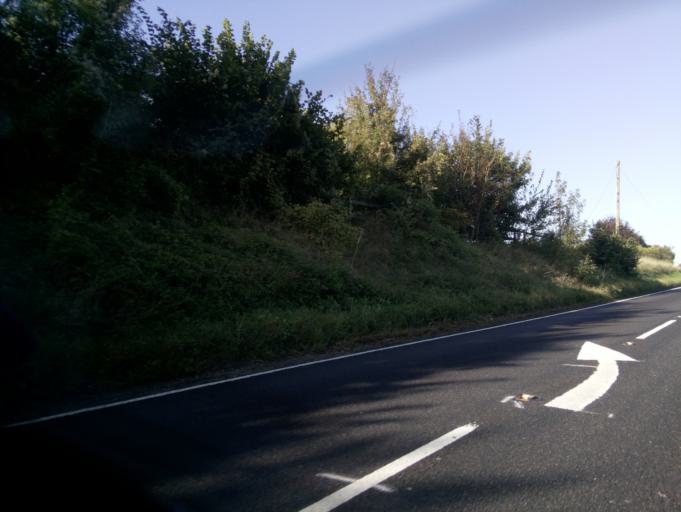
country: GB
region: England
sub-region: Hampshire
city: Four Marks
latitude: 51.0139
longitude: -1.0855
